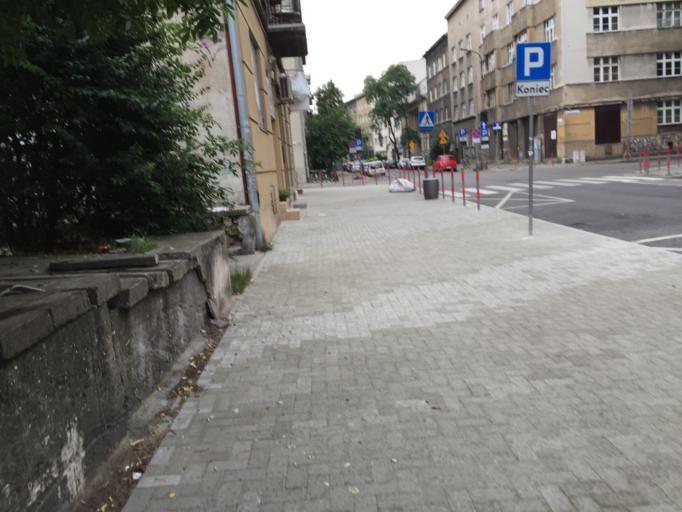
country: PL
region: Lesser Poland Voivodeship
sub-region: Krakow
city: Krakow
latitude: 50.0700
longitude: 19.9204
